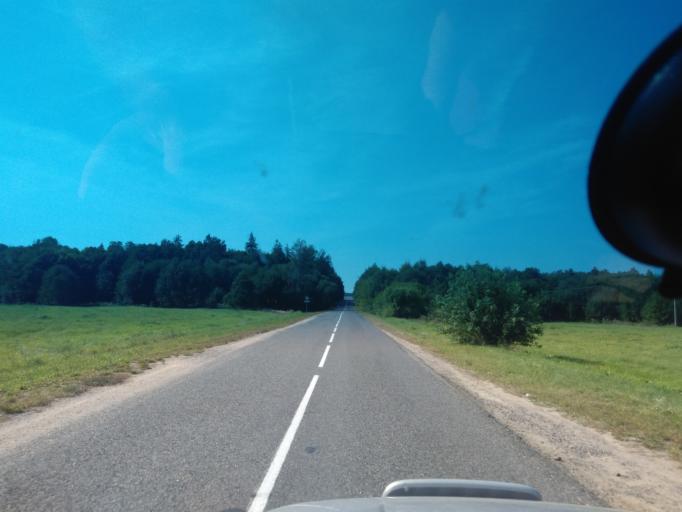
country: BY
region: Minsk
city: Kapyl'
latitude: 53.2244
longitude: 27.1625
